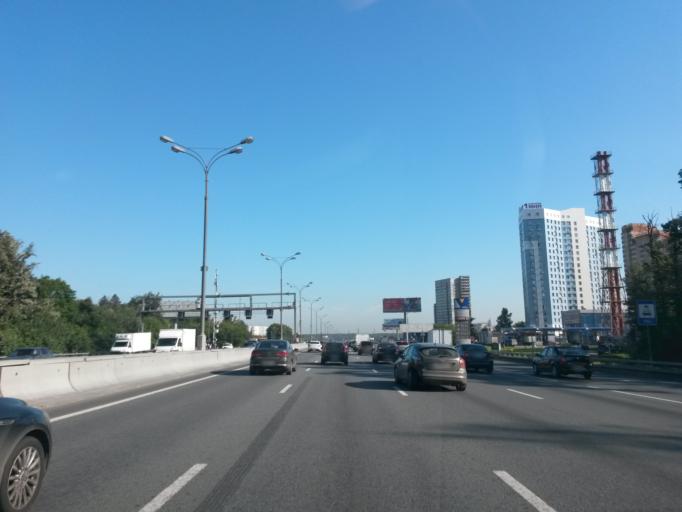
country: RU
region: Moscow
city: Vostochnyy
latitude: 55.8018
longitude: 37.8402
